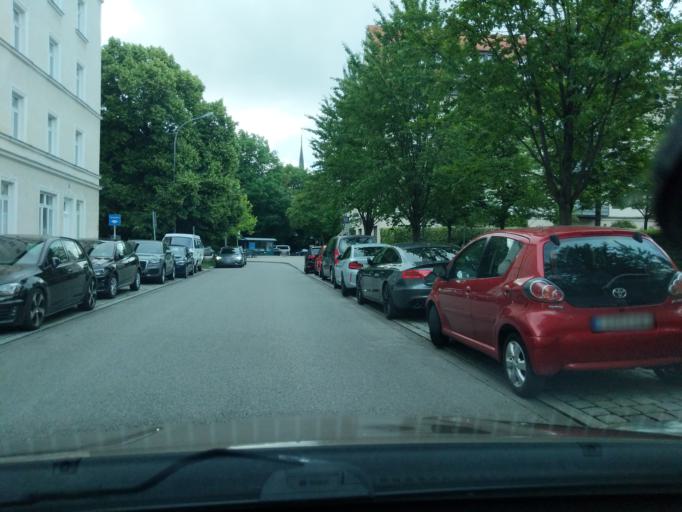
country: DE
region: Bavaria
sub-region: Upper Bavaria
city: Bogenhausen
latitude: 48.1317
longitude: 11.6059
